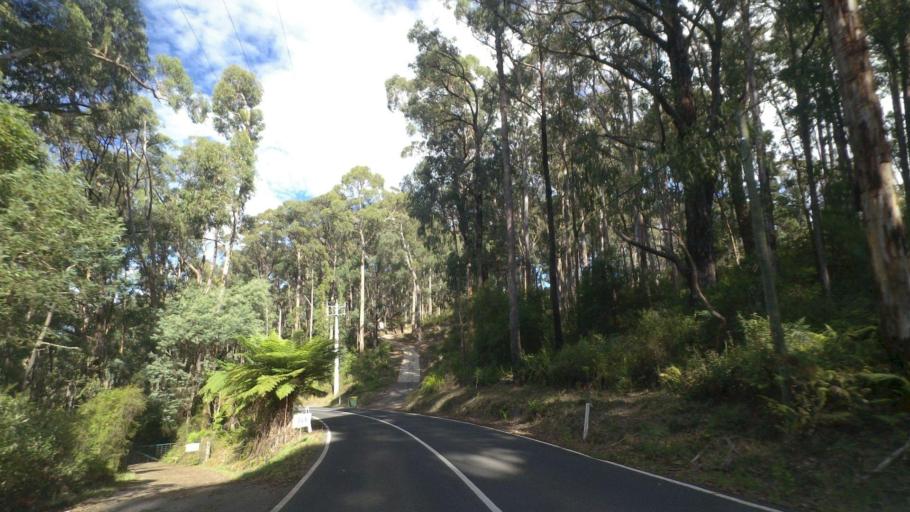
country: AU
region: Victoria
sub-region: Cardinia
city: Gembrook
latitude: -37.9739
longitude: 145.5784
